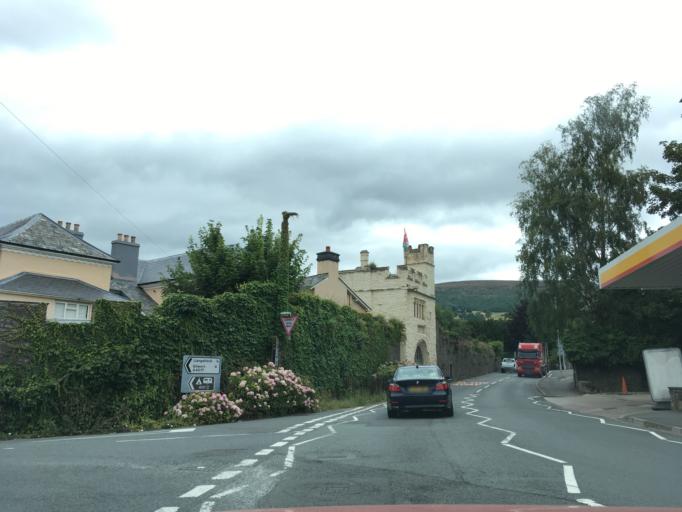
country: GB
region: Wales
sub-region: Monmouthshire
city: Gilwern
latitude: 51.8599
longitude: -3.1375
